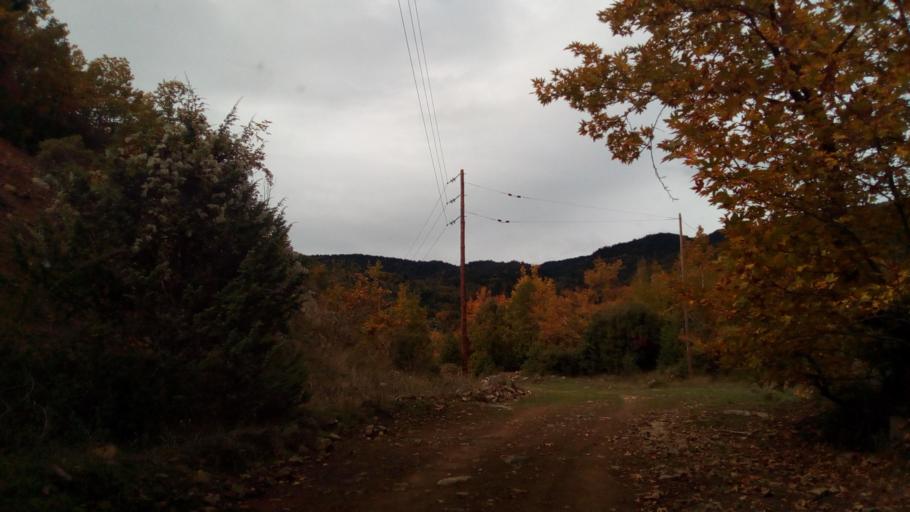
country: GR
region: West Greece
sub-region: Nomos Aitolias kai Akarnanias
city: Nafpaktos
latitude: 38.5596
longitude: 21.9617
